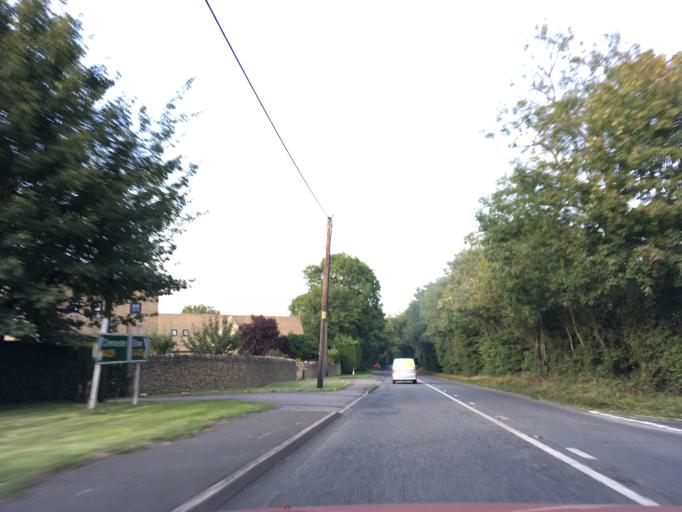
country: GB
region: England
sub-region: Gloucestershire
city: Bourton on the Water
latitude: 51.8818
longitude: -1.7759
